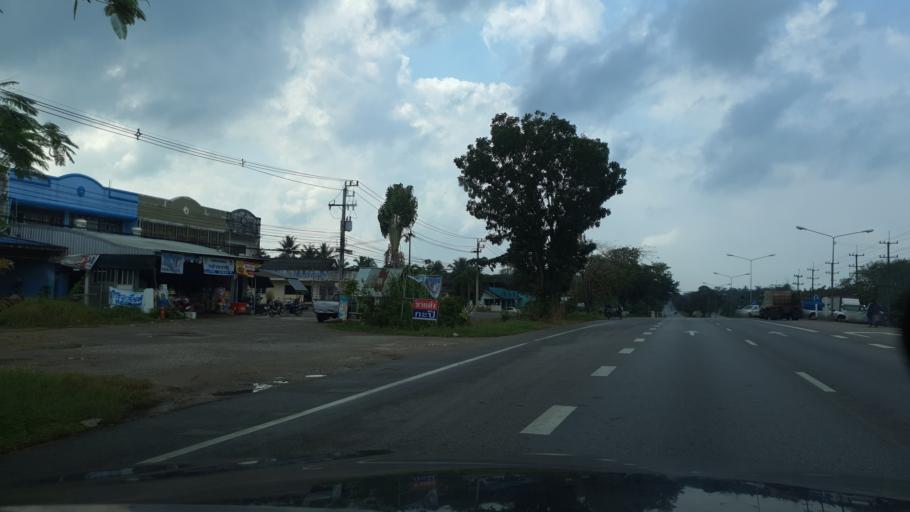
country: TH
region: Chumphon
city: Pathio
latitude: 10.9162
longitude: 99.2820
